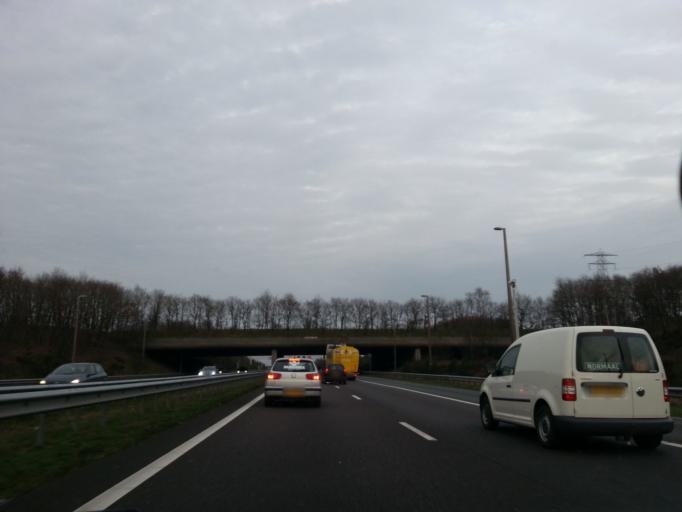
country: NL
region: Gelderland
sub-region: Gemeente Rozendaal
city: Rozendaal
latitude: 52.0647
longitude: 5.9431
